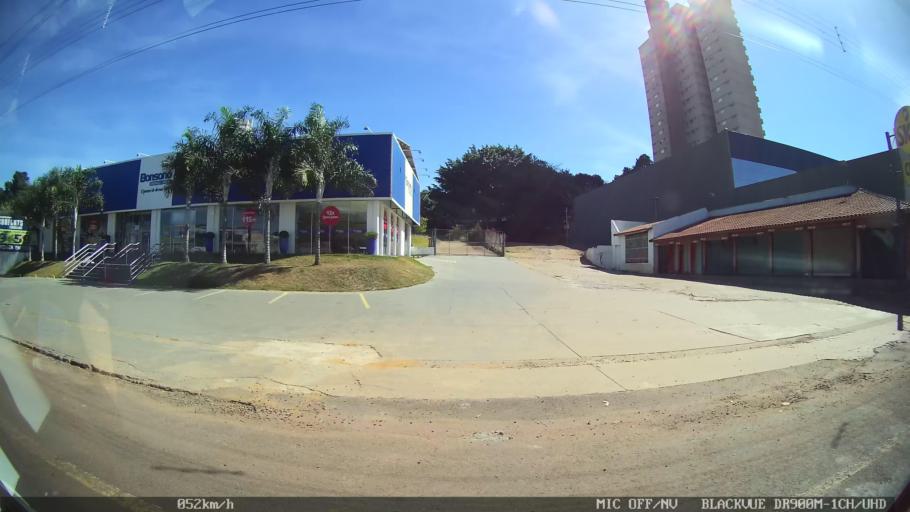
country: BR
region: Sao Paulo
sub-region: Franca
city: Franca
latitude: -20.5421
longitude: -47.3960
